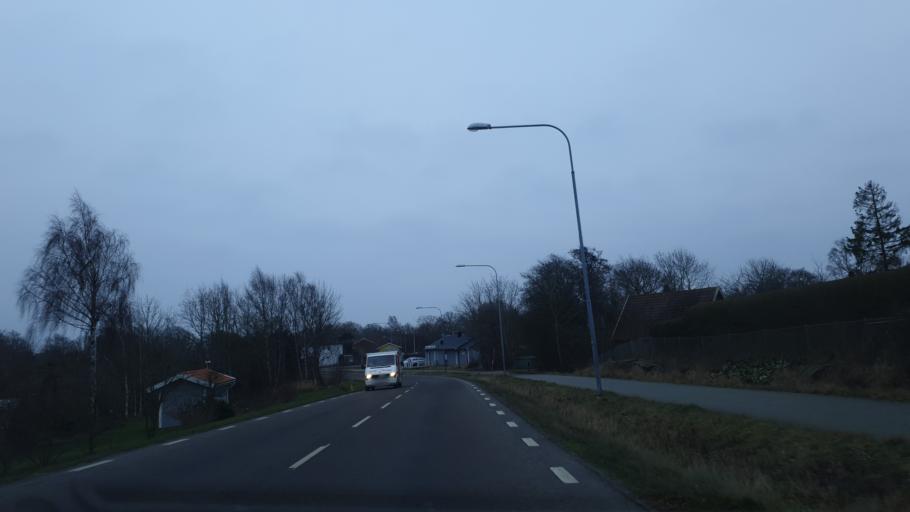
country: SE
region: Blekinge
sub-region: Karlskrona Kommun
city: Sturko
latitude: 56.1139
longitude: 15.6740
